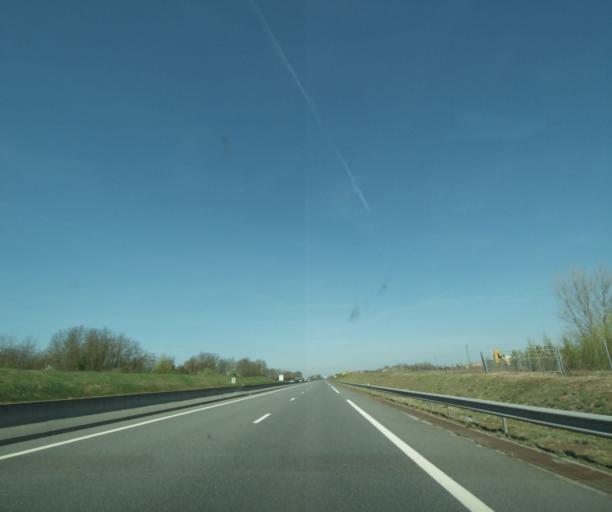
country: FR
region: Auvergne
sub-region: Departement de l'Allier
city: Trevol
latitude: 46.6083
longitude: 3.2949
